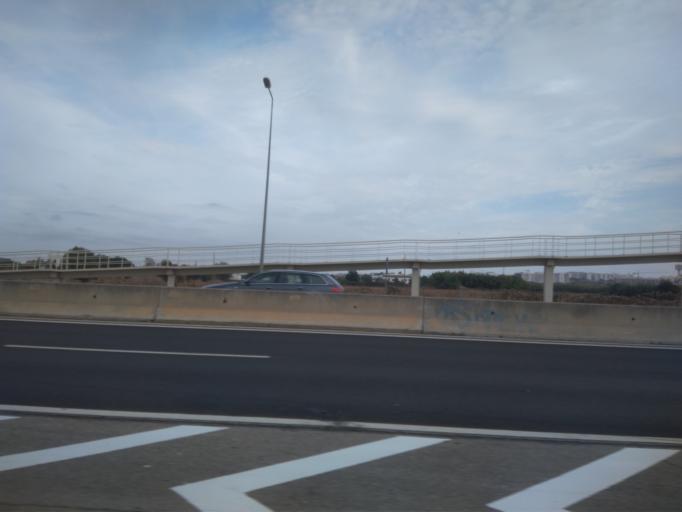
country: PT
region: Faro
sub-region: Faro
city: Faro
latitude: 37.0367
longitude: -7.9501
